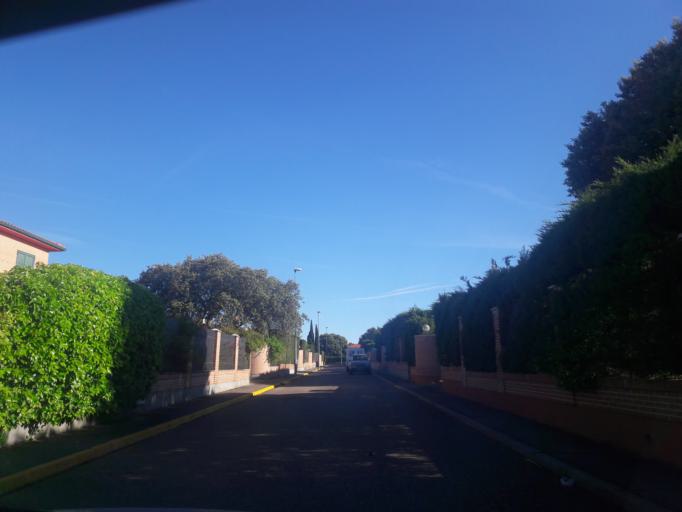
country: ES
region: Castille and Leon
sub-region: Provincia de Salamanca
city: Martinamor
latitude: 40.8057
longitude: -5.6364
